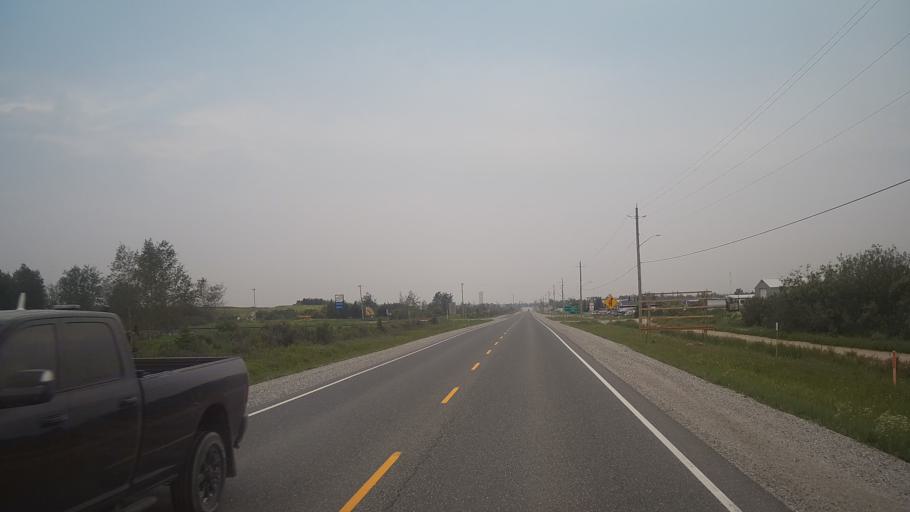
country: CA
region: Ontario
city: Hearst
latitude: 49.6828
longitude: -83.6204
